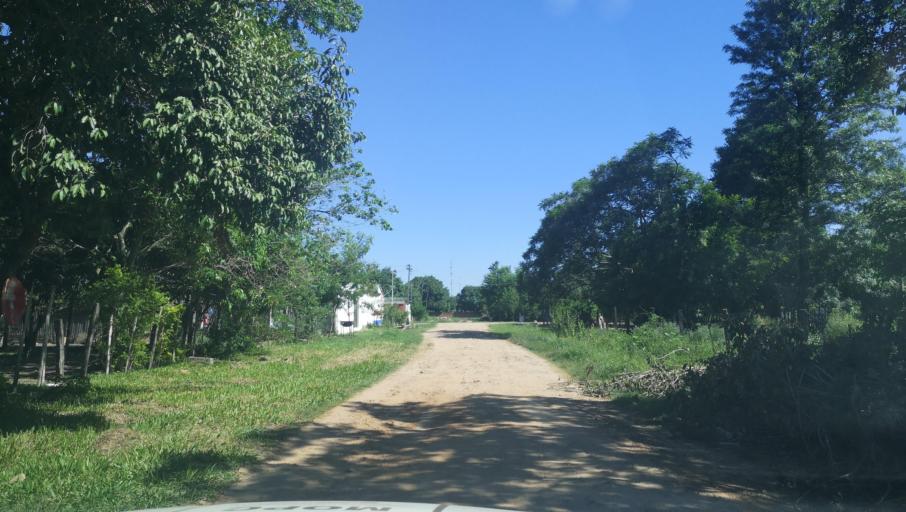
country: PY
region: Caaguazu
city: Carayao
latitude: -25.1977
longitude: -56.3940
